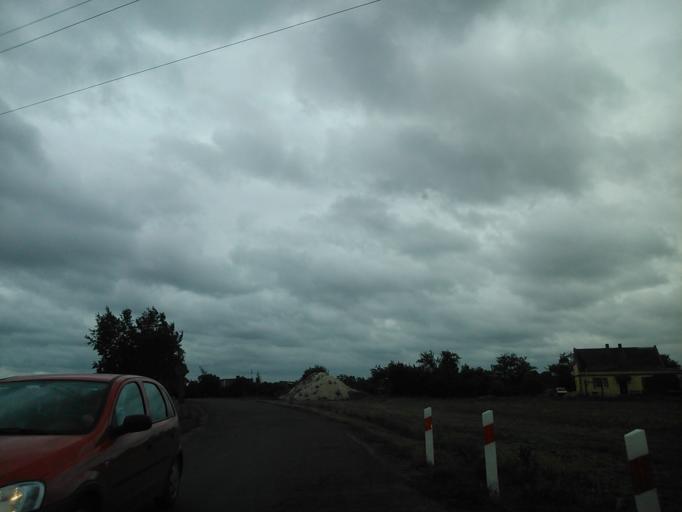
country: PL
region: Kujawsko-Pomorskie
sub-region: Powiat inowroclawski
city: Inowroclaw
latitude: 52.7473
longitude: 18.3135
